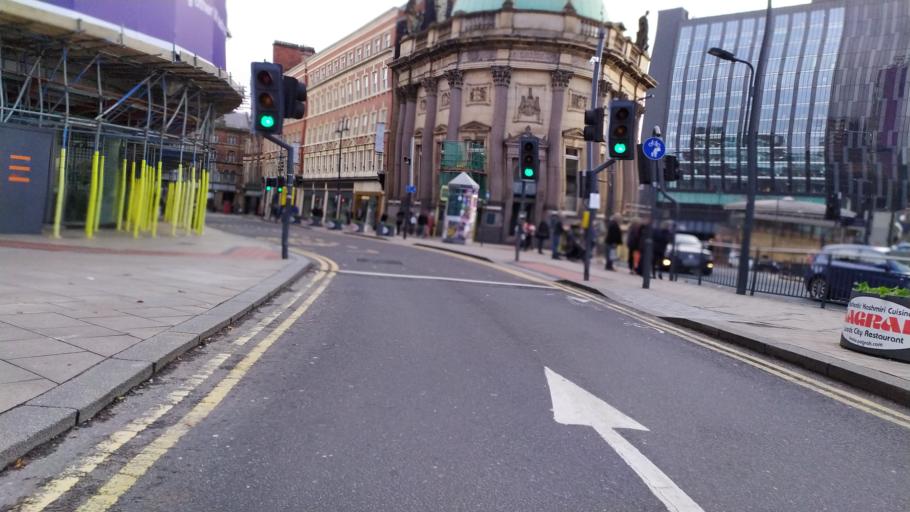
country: GB
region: England
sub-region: City and Borough of Leeds
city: Leeds
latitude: 53.7964
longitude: -1.5471
